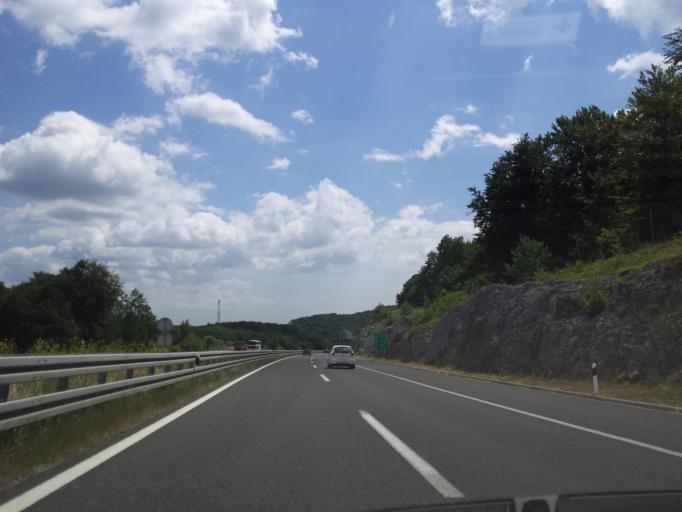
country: HR
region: Primorsko-Goranska
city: Vrbovsko
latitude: 45.3855
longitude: 15.1768
